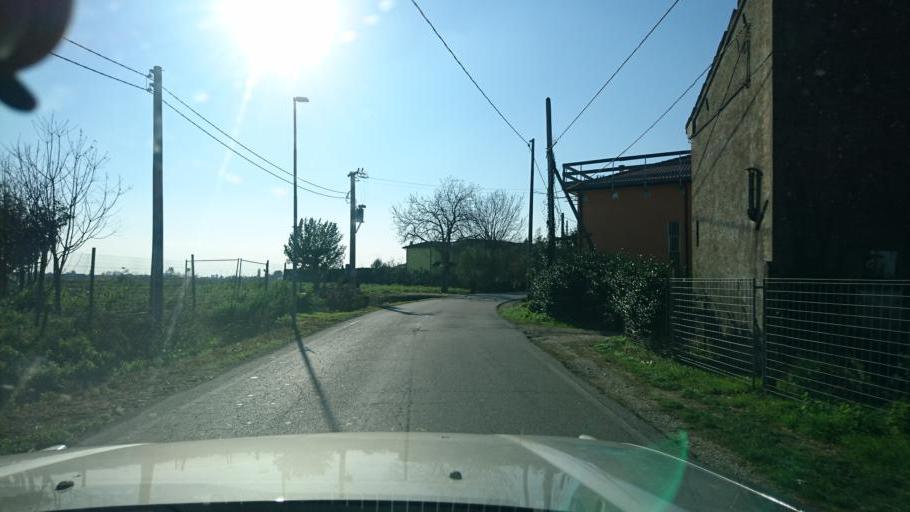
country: IT
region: Veneto
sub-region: Provincia di Padova
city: Carceri
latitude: 45.2060
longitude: 11.6163
